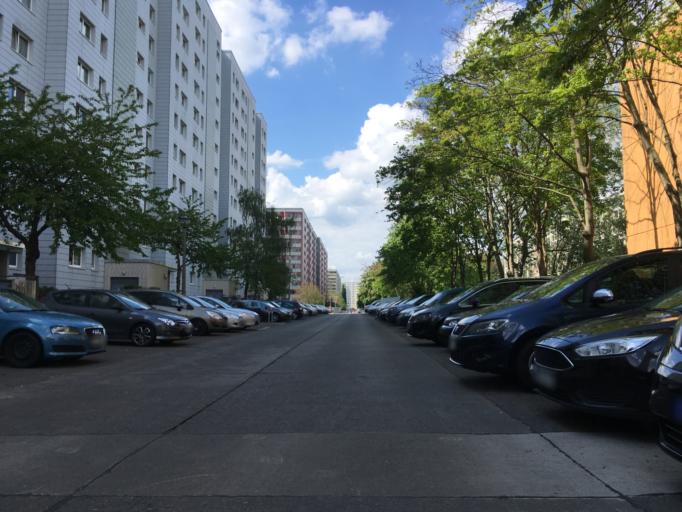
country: DE
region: Berlin
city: Neu-Hohenschoenhausen
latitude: 52.5670
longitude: 13.5072
